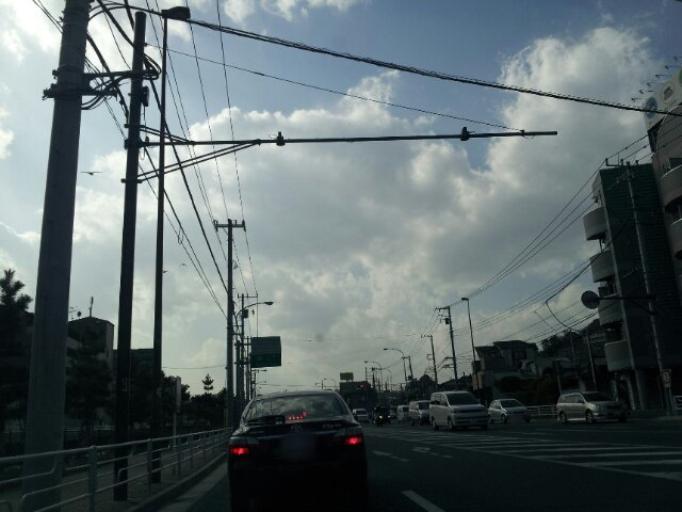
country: JP
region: Kanagawa
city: Yokohama
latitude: 35.4454
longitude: 139.5883
